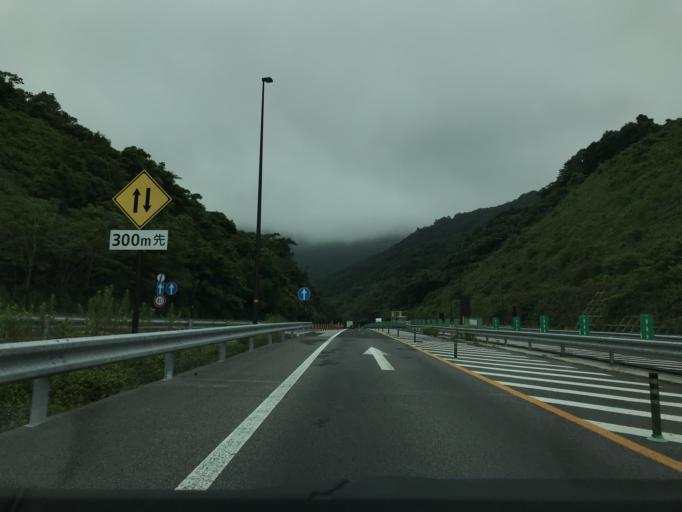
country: JP
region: Oita
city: Bungo-Takada-shi
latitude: 33.4965
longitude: 131.3182
